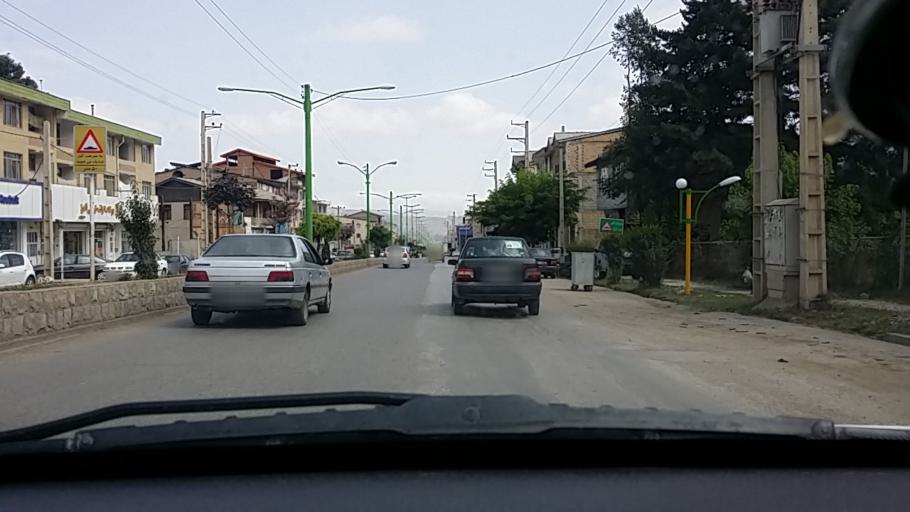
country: IR
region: Mazandaran
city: `Abbasabad
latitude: 36.5076
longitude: 51.1709
